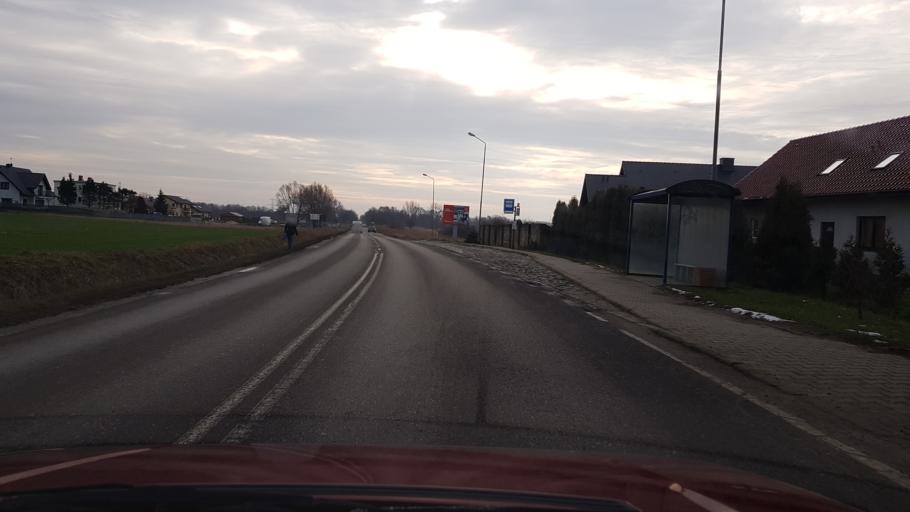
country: PL
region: West Pomeranian Voivodeship
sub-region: Powiat policki
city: Police
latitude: 53.5094
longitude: 14.5699
